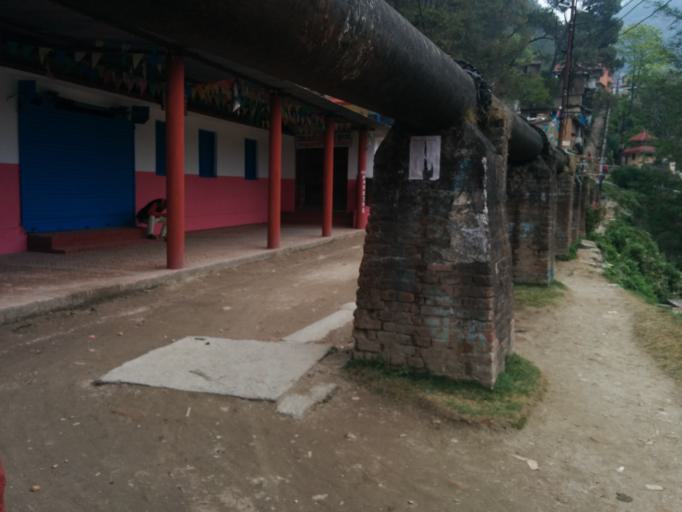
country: NP
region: Central Region
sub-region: Bagmati Zone
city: Bhaktapur
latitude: 27.7609
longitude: 85.4212
